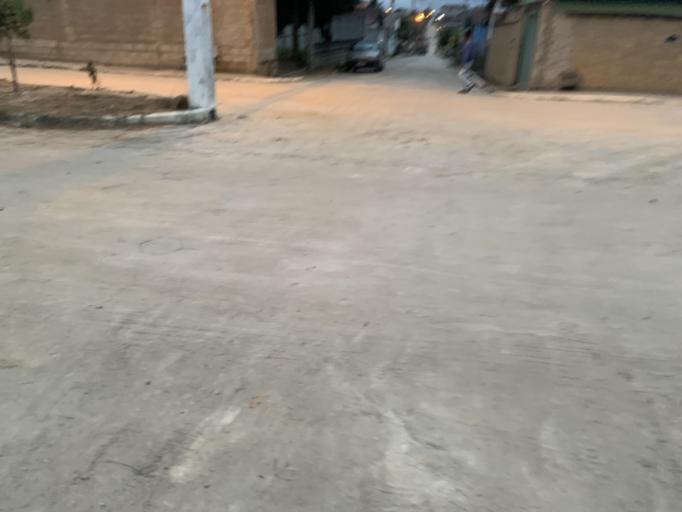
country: BR
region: Bahia
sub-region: Medeiros Neto
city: Medeiros Neto
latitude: -17.3896
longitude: -40.2324
